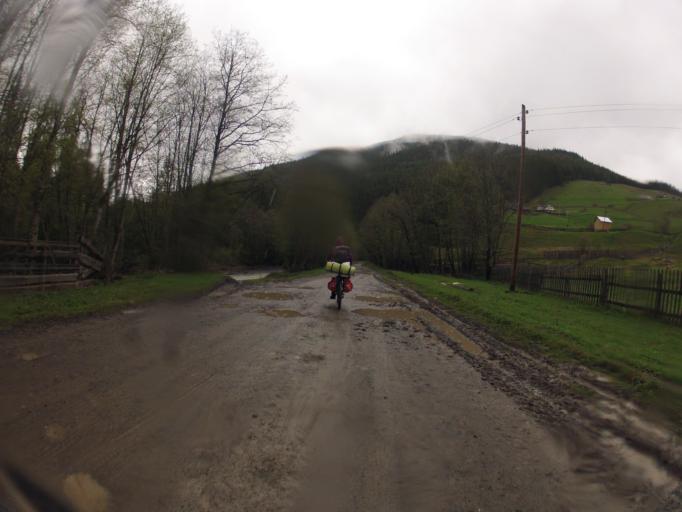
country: RO
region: Suceava
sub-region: Comuna Izvoarele Sucevei
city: Izvoarele Sucevei
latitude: 47.8332
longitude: 25.0486
